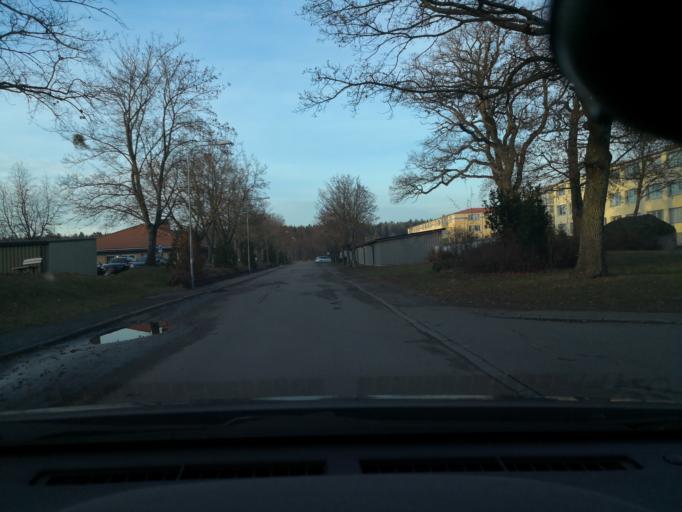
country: SE
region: Vaestmanland
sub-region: Vasteras
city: Vasteras
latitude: 59.6107
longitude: 16.4912
